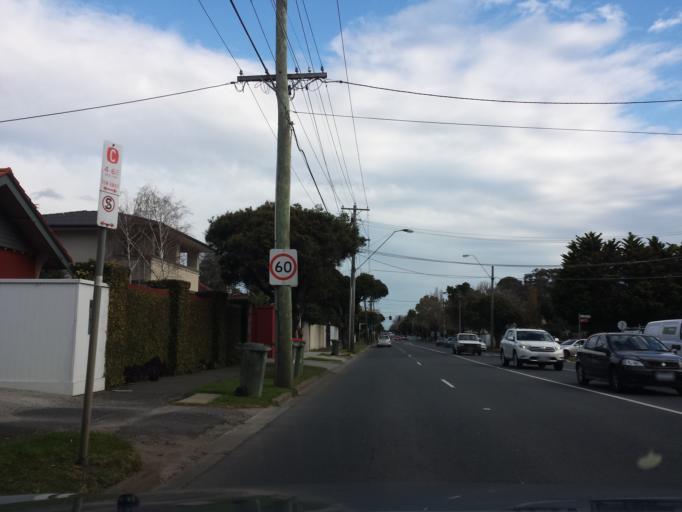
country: AU
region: Victoria
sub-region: Port Phillip
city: Elwood
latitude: -37.8960
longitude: 144.9899
